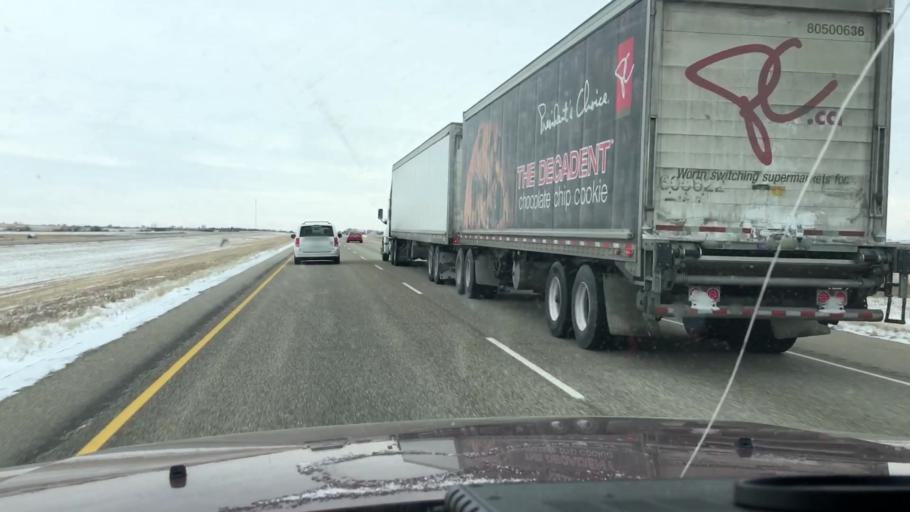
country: CA
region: Saskatchewan
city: Saskatoon
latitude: 51.5184
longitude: -106.2905
